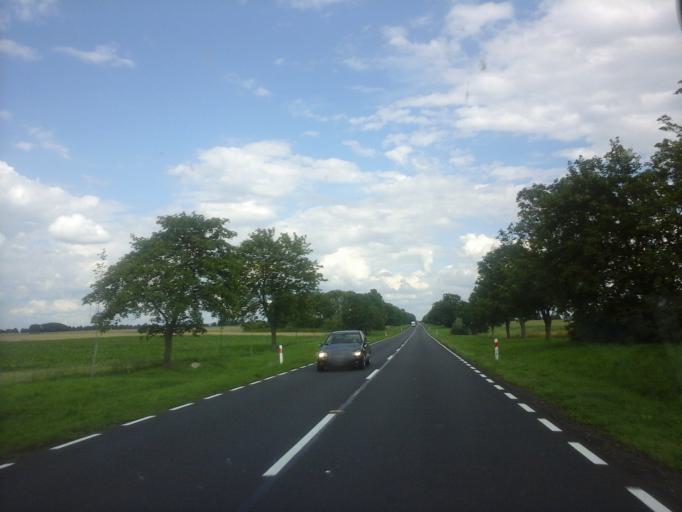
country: PL
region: West Pomeranian Voivodeship
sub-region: Powiat stargardzki
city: Dolice
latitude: 53.2921
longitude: 15.2148
